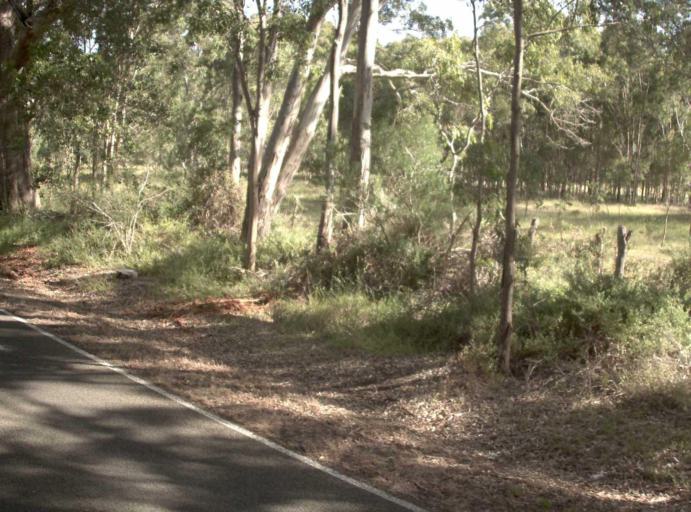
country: AU
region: Victoria
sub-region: East Gippsland
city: Lakes Entrance
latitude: -37.8046
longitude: 147.8393
